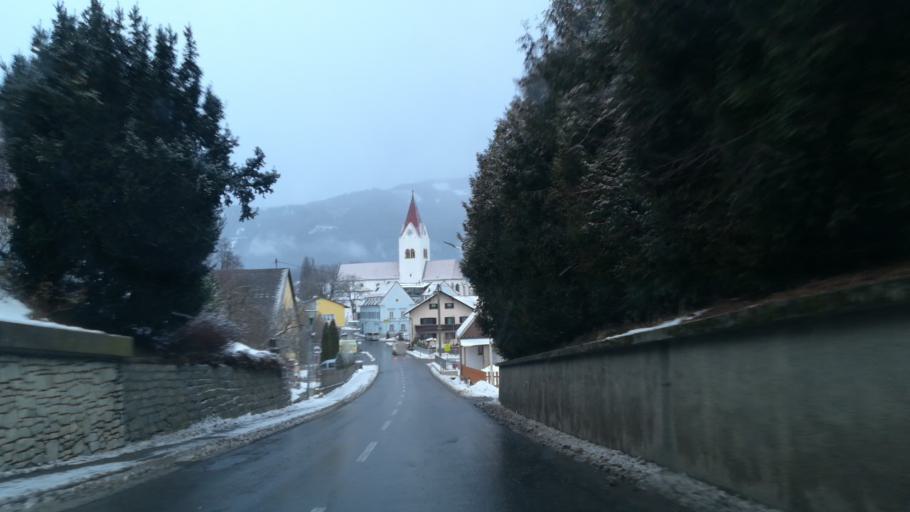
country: AT
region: Styria
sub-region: Politischer Bezirk Murtal
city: Poels
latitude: 47.2182
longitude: 14.5811
